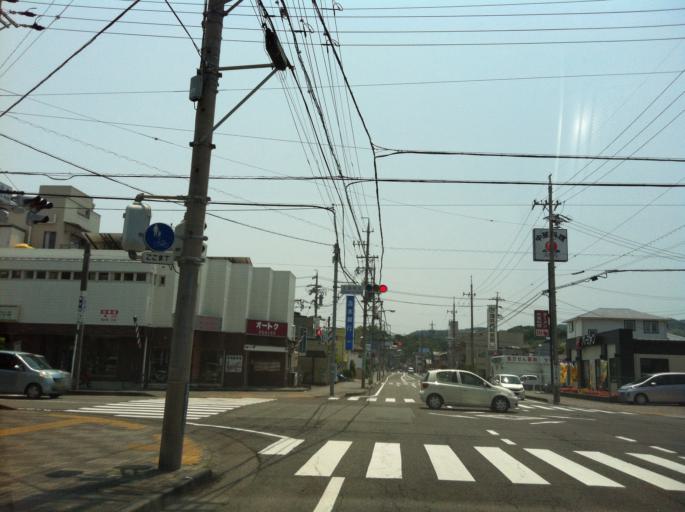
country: JP
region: Shizuoka
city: Shizuoka-shi
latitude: 35.0013
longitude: 138.4819
